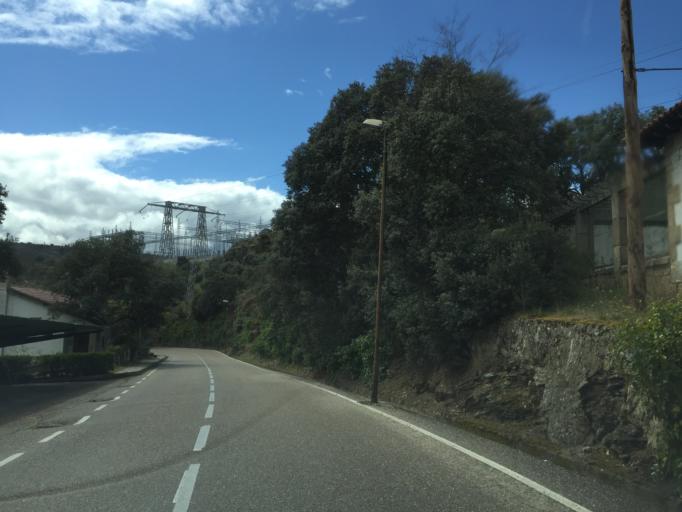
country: ES
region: Castille and Leon
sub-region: Provincia de Zamora
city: Moral de Sayago
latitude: 41.4935
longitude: -6.0881
